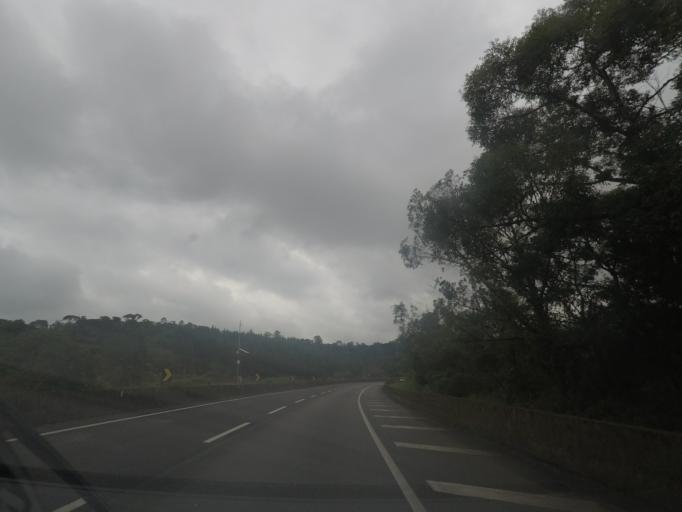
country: BR
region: Sao Paulo
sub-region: Cajati
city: Cajati
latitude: -24.9714
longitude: -48.3697
